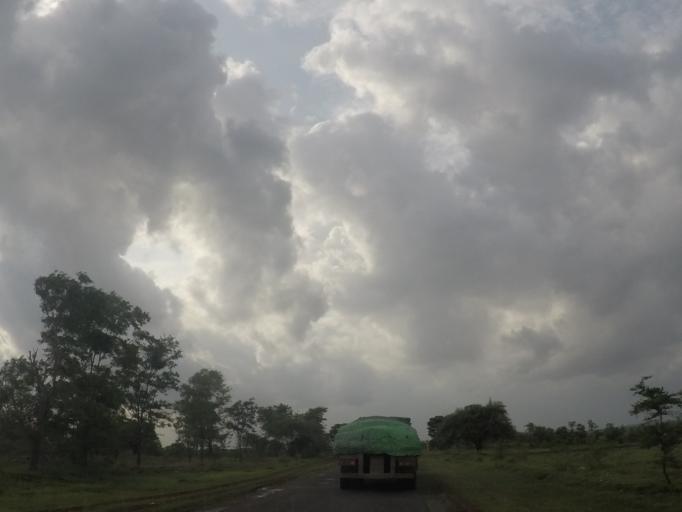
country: MM
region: Mandalay
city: Meiktila
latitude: 20.5384
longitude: 95.6857
